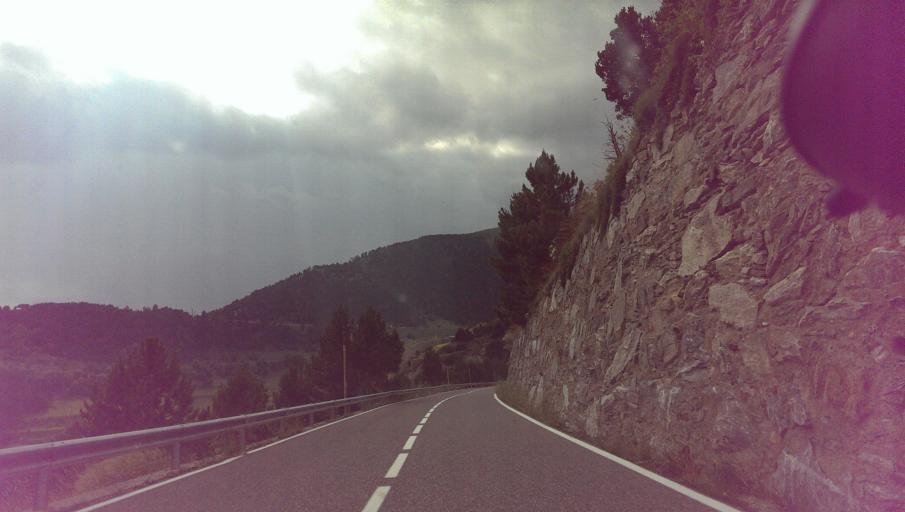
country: AD
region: Canillo
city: Canillo
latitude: 42.5724
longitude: 1.5984
